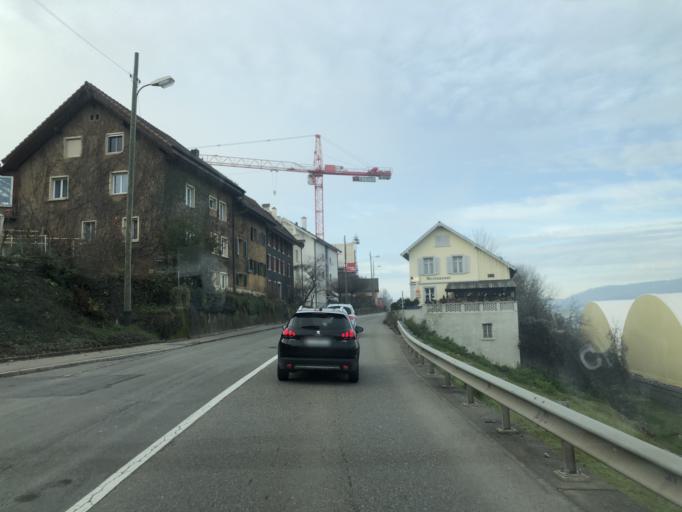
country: CH
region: Aargau
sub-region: Bezirk Baden
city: Turgi
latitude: 47.4864
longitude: 8.2655
